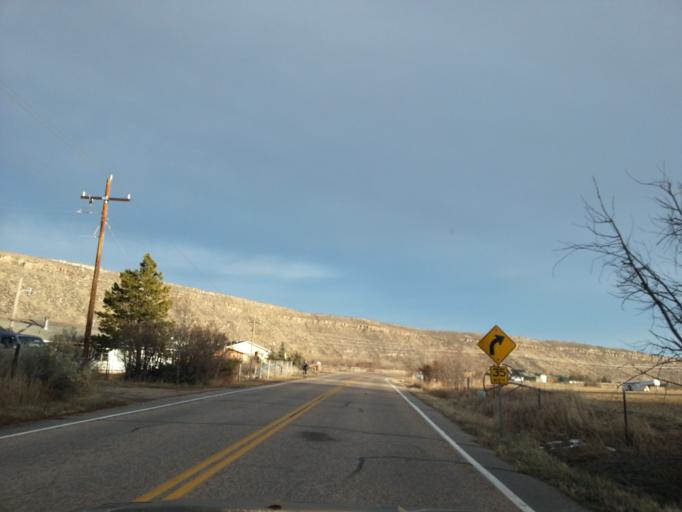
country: US
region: Colorado
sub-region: Larimer County
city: Loveland
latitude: 40.4686
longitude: -105.2086
